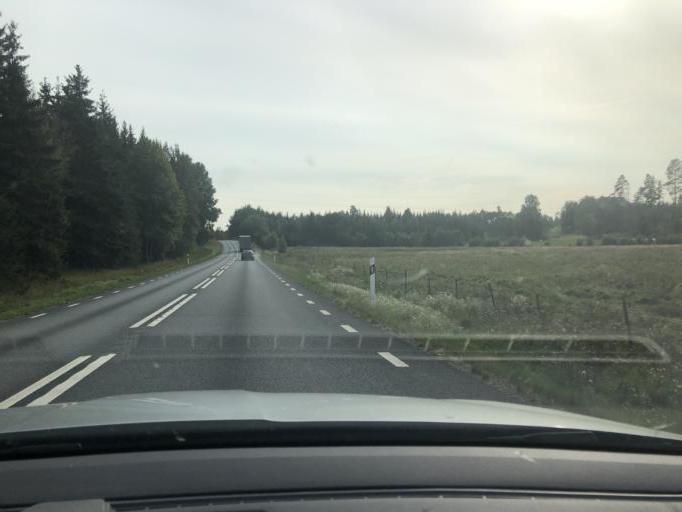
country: SE
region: Joenkoeping
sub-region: Vetlanda Kommun
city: Ekenassjon
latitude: 57.5298
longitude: 14.9902
